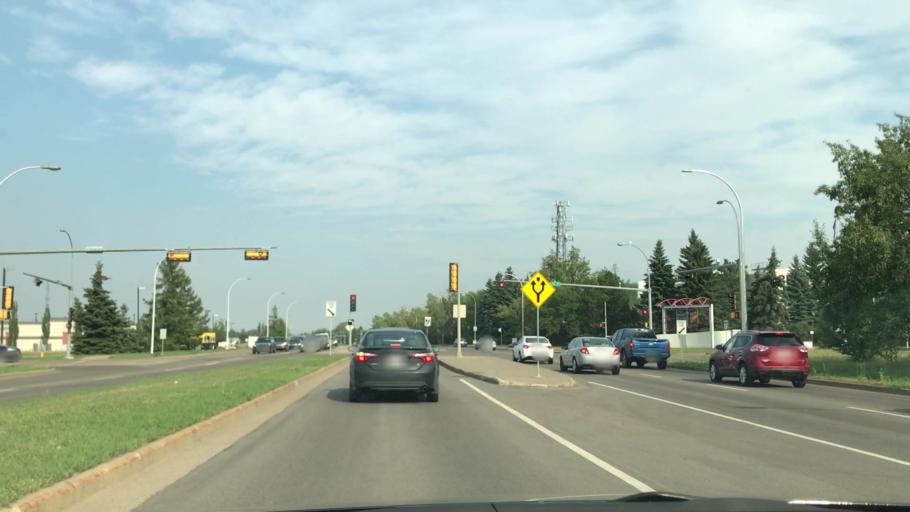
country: CA
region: Alberta
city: Edmonton
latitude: 53.4520
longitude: -113.4741
